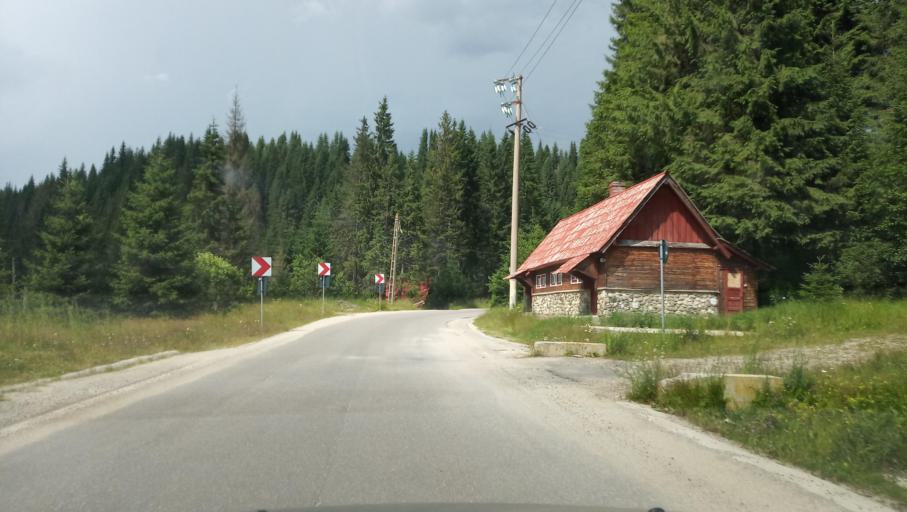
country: RO
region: Dambovita
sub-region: Comuna Moroeni
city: Glod
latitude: 45.3334
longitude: 25.4297
